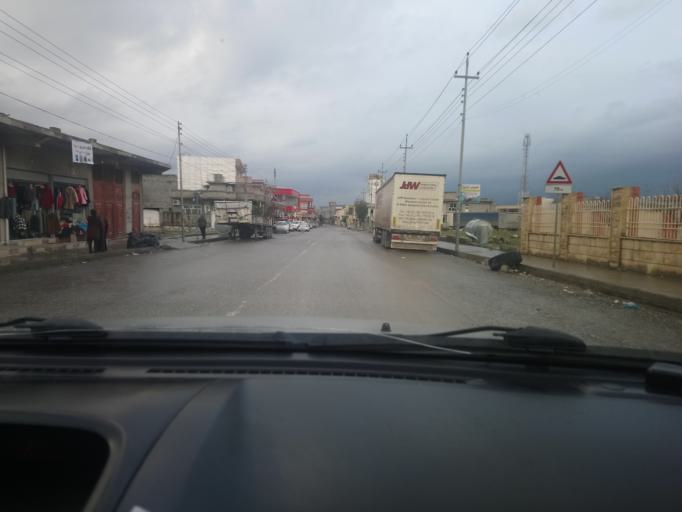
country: IQ
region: As Sulaymaniyah
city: Qeladize
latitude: 36.1819
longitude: 45.1361
